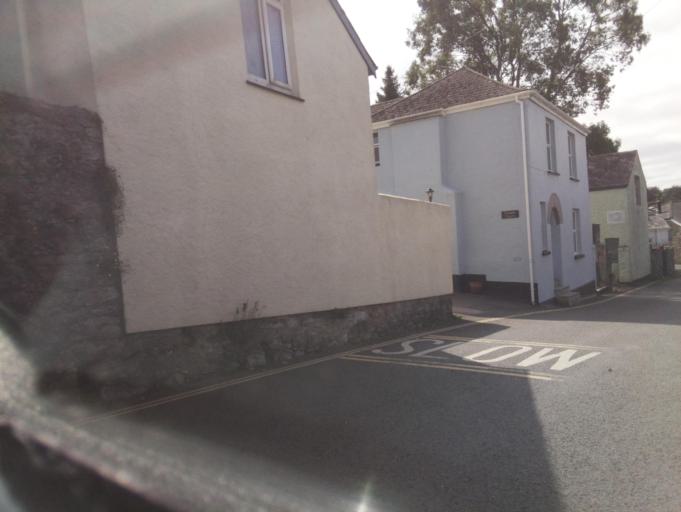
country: GB
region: England
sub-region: Devon
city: Marldon
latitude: 50.4068
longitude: -3.6239
